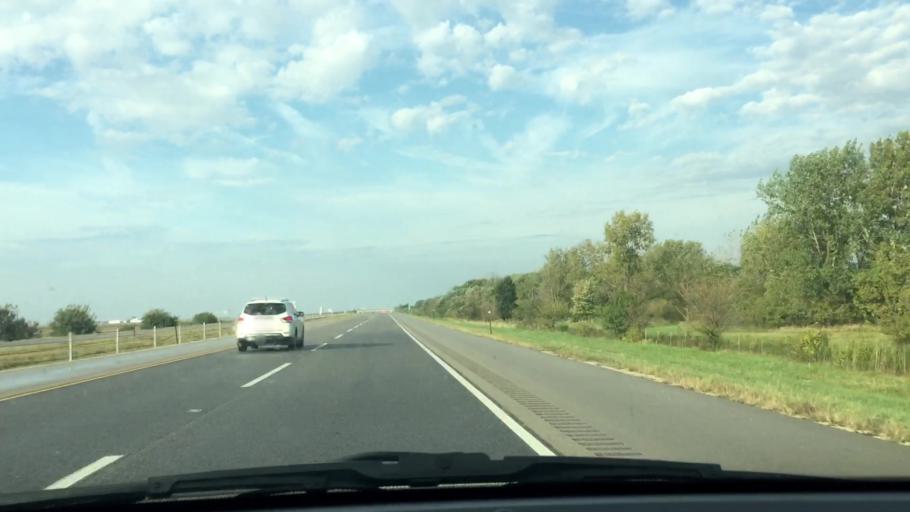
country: US
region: Illinois
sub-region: Ogle County
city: Rochelle
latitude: 41.8906
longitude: -89.0939
